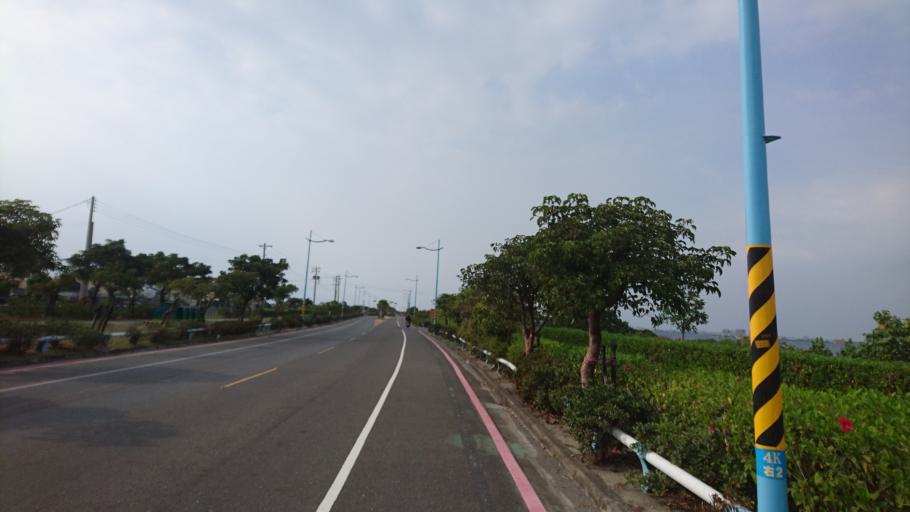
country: TW
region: Taiwan
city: Fengshan
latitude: 22.4324
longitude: 120.4854
